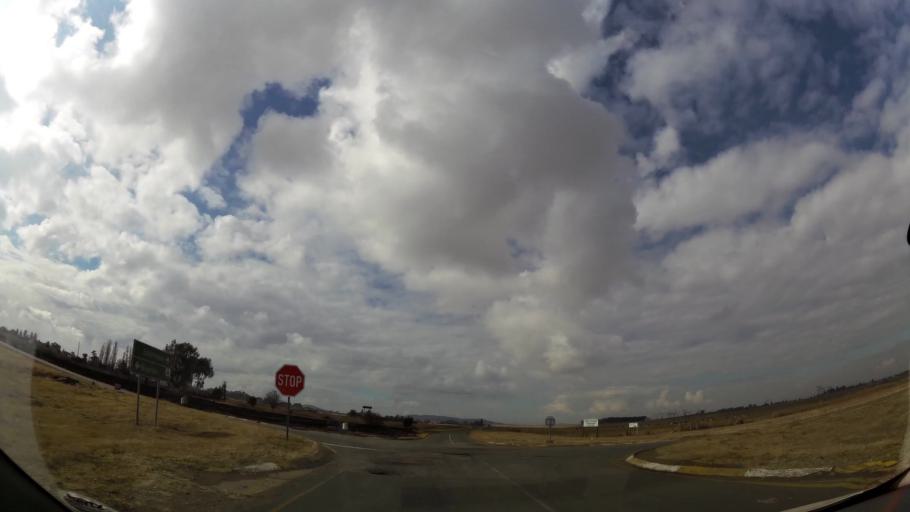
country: ZA
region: Gauteng
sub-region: Sedibeng District Municipality
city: Meyerton
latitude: -26.6193
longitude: 28.0573
